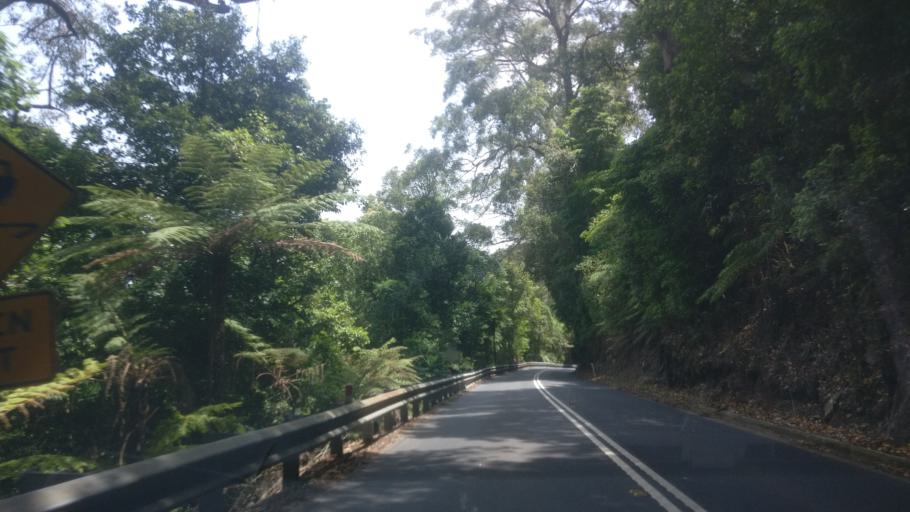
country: AU
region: New South Wales
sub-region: Shoalhaven Shire
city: Kangaroo Valley
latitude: -34.7899
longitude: 150.5642
